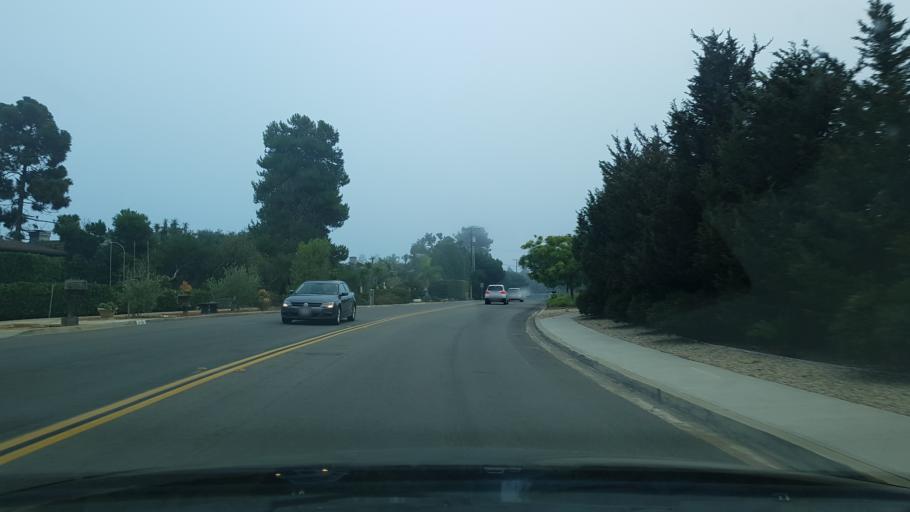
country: US
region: California
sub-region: San Diego County
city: La Jolla
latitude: 32.8542
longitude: -117.2398
